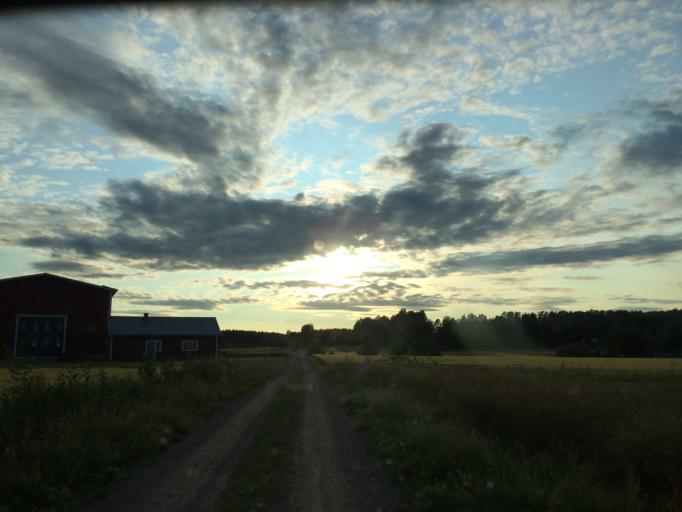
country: FI
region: Haeme
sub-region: Haemeenlinna
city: Turenki
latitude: 60.8861
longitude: 24.6288
